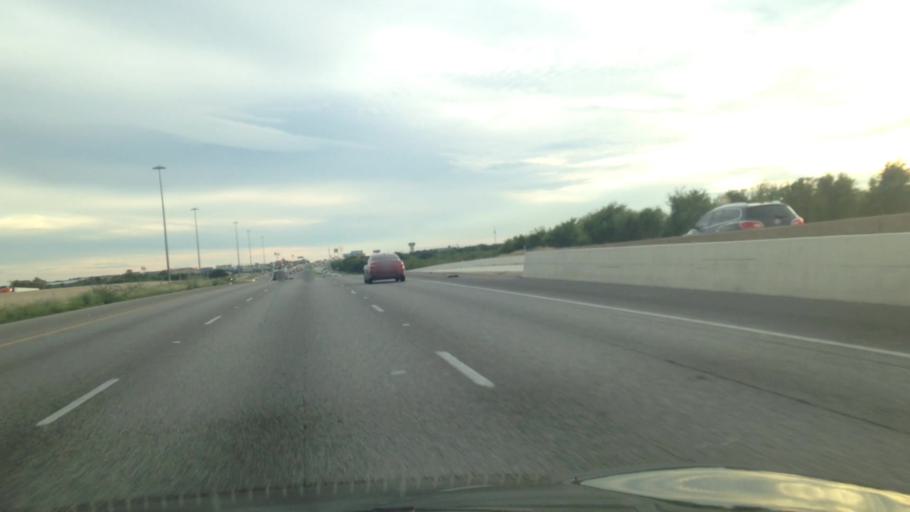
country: US
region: Texas
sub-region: Hays County
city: Buda
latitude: 30.1050
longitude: -97.8106
